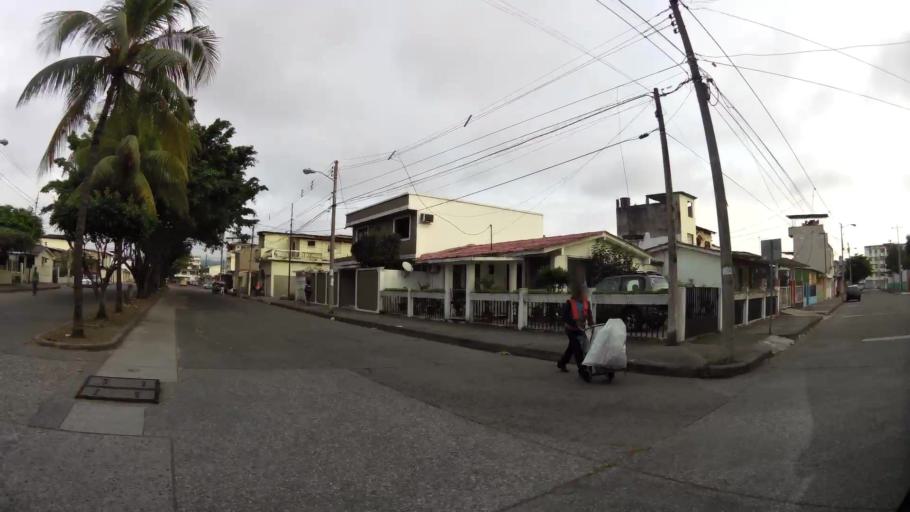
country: EC
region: Guayas
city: Eloy Alfaro
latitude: -2.1732
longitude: -79.8857
